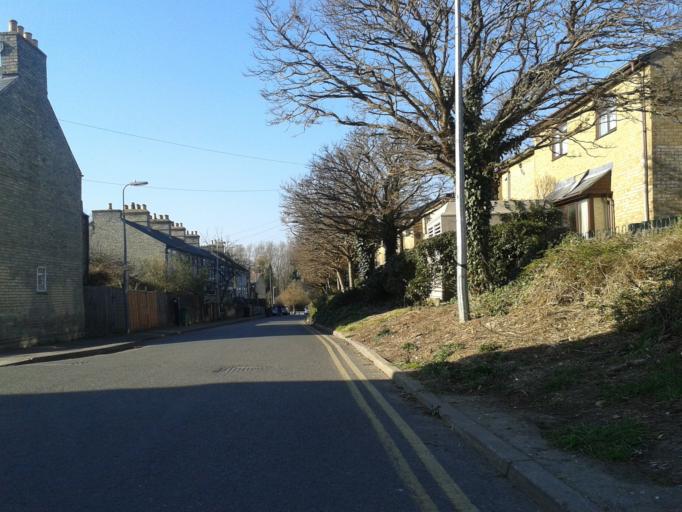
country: GB
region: England
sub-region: Cambridgeshire
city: Cambridge
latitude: 52.2104
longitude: 0.1422
